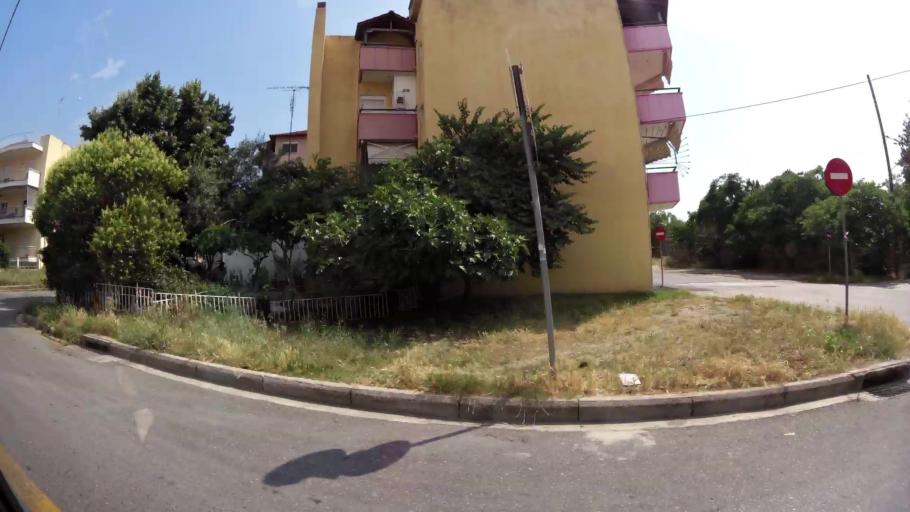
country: GR
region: Central Macedonia
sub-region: Nomos Thessalonikis
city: Polichni
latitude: 40.6674
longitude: 22.9438
